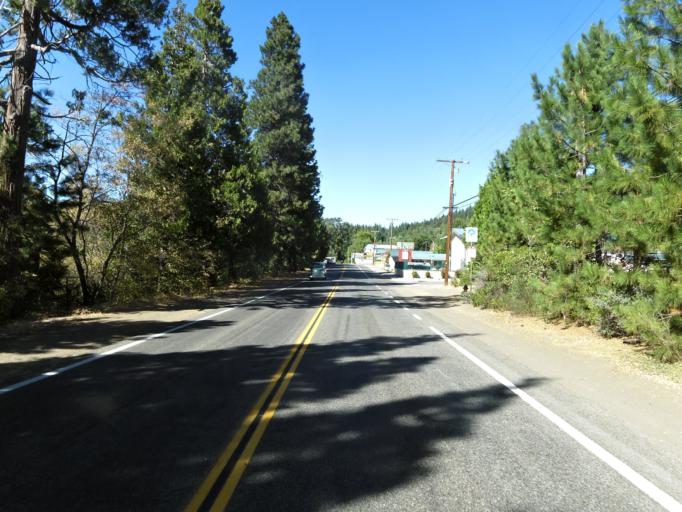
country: US
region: California
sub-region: Siskiyou County
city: Mount Shasta
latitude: 41.2999
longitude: -122.3062
